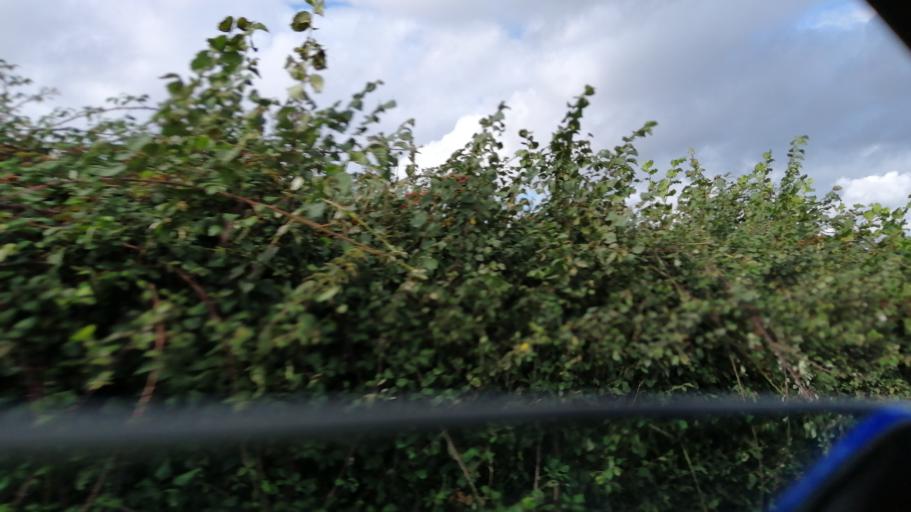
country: GB
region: England
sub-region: Herefordshire
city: Callow
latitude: 52.0100
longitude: -2.7484
